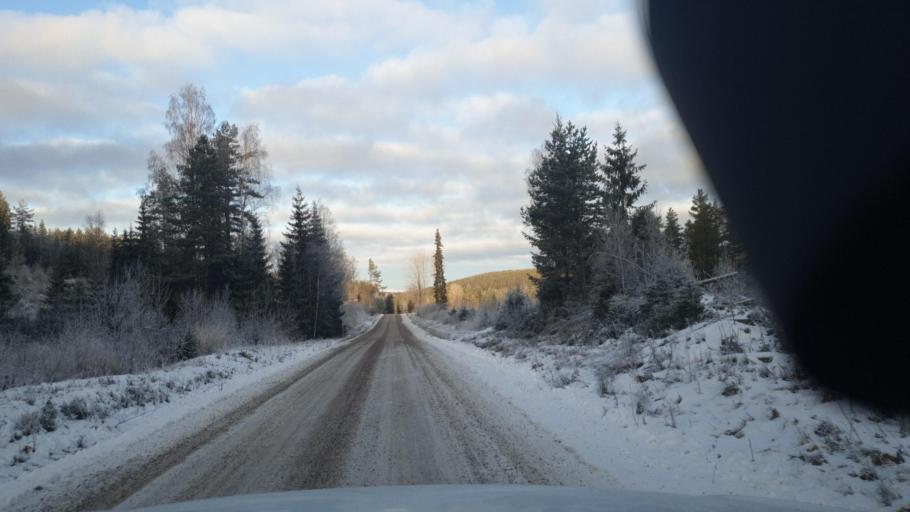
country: SE
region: Vaermland
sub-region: Eda Kommun
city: Charlottenberg
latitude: 60.0775
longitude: 12.5253
